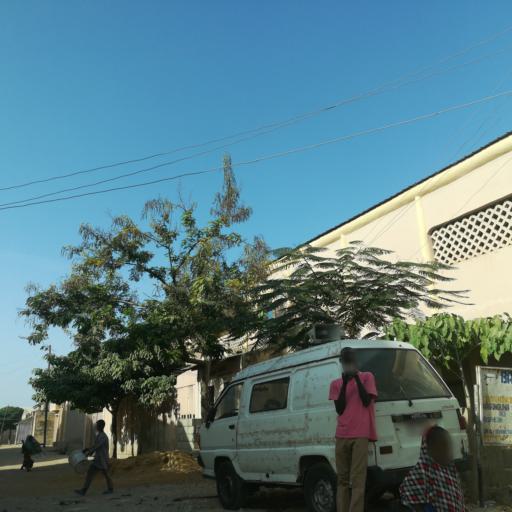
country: NG
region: Kano
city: Kano
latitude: 12.0150
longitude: 8.4987
